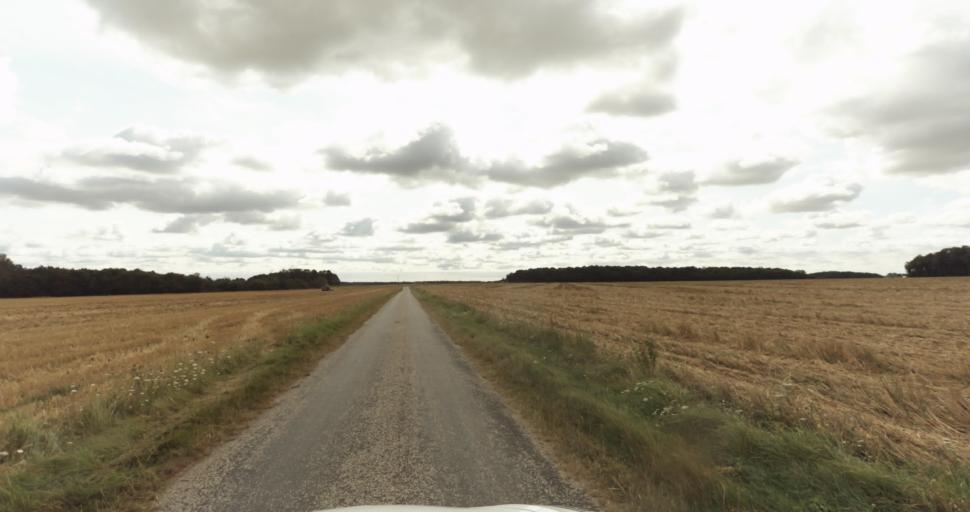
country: FR
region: Haute-Normandie
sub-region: Departement de l'Eure
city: Nonancourt
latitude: 48.7946
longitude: 1.1364
